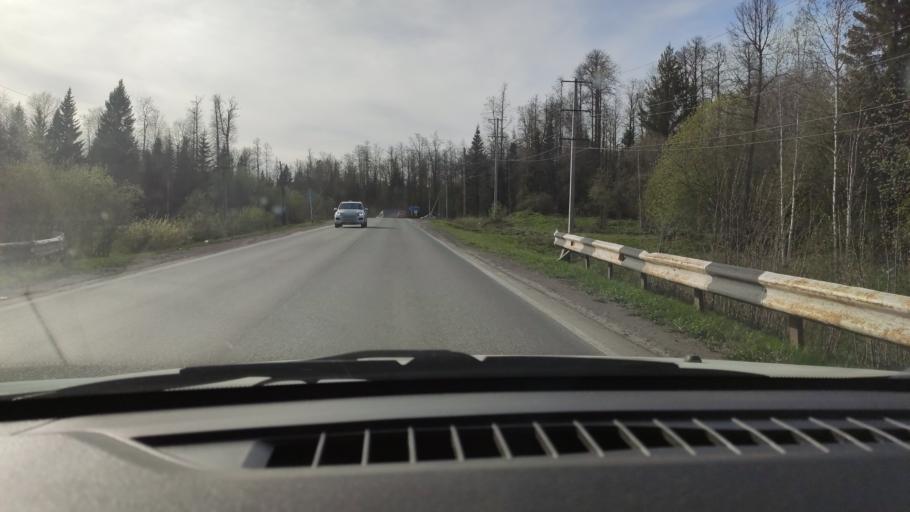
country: RU
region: Perm
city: Novyye Lyady
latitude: 57.9544
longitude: 56.5179
